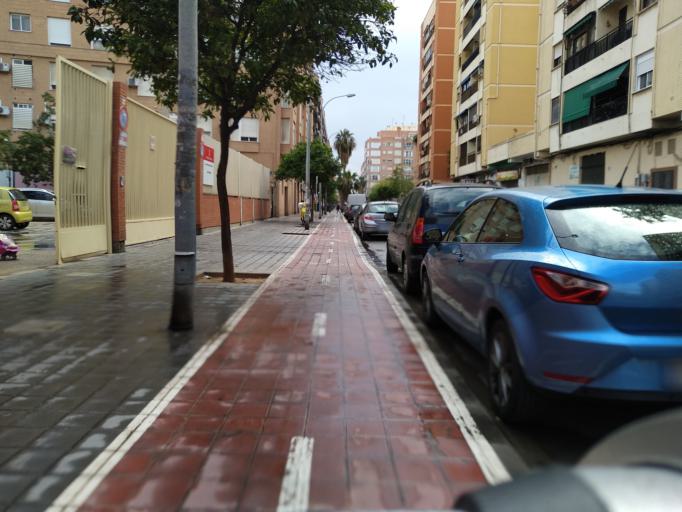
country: ES
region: Valencia
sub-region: Provincia de Valencia
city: Alboraya
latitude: 39.4681
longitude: -0.3366
